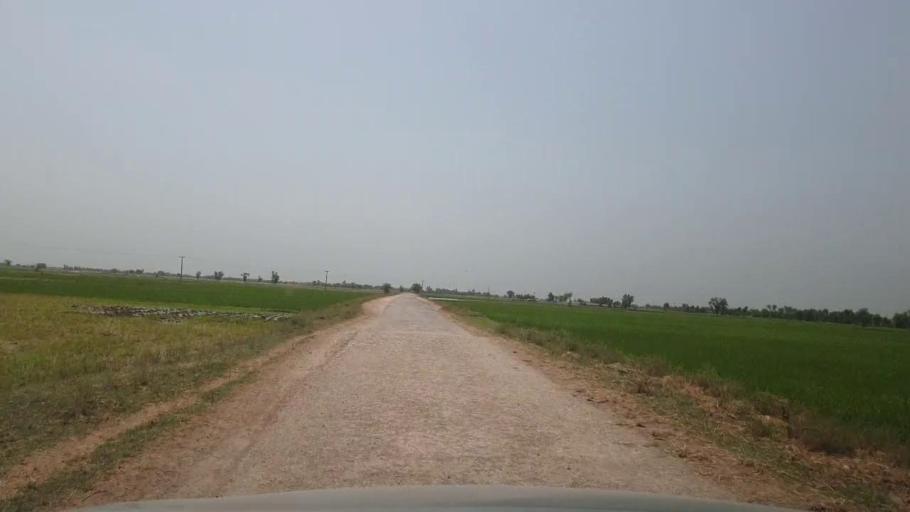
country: PK
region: Sindh
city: Garhi Yasin
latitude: 27.9197
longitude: 68.4040
